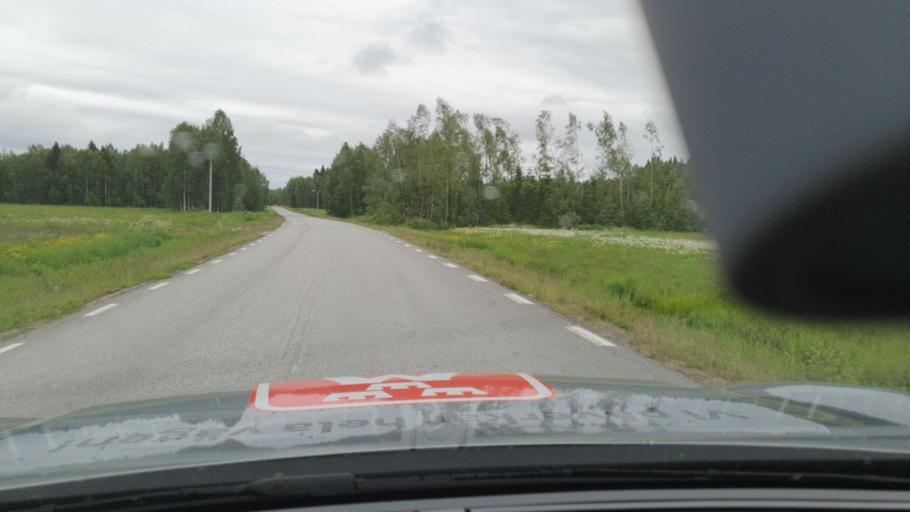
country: SE
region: Norrbotten
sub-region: Kalix Kommun
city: Toere
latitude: 65.8612
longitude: 22.6757
